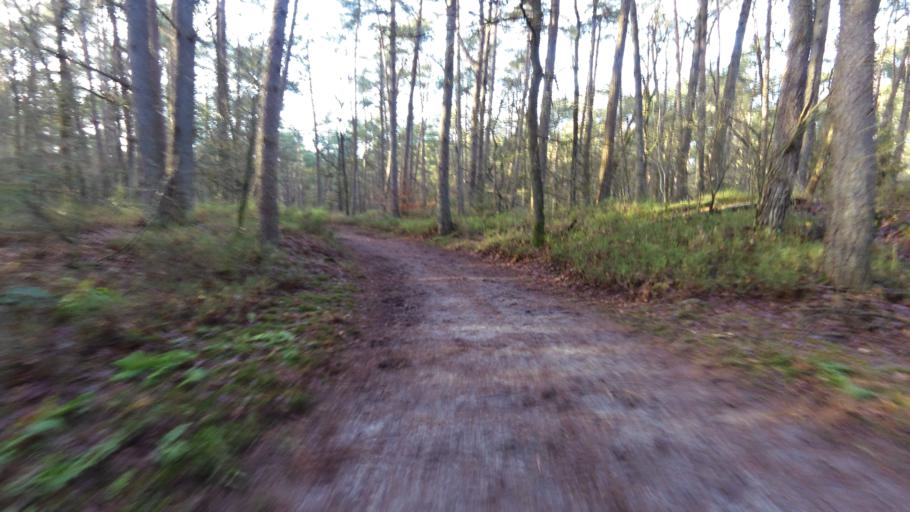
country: NL
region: Gelderland
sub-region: Gemeente Epe
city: Vaassen
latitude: 52.2649
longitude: 5.9318
